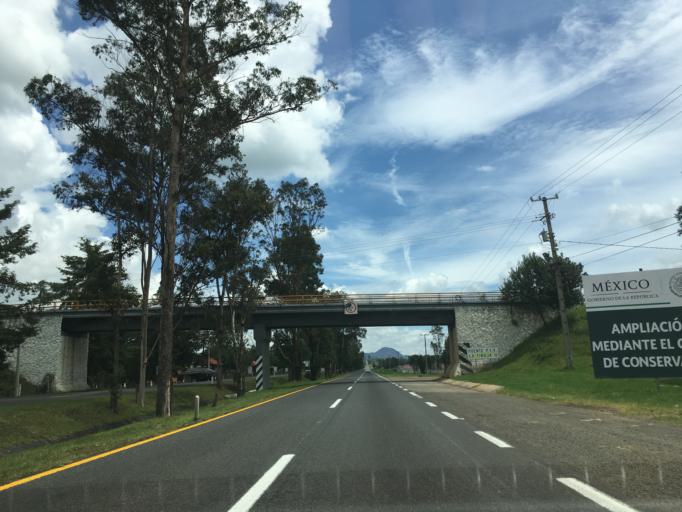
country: MX
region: Michoacan
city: Cuanajo
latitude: 19.5373
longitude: -101.5240
